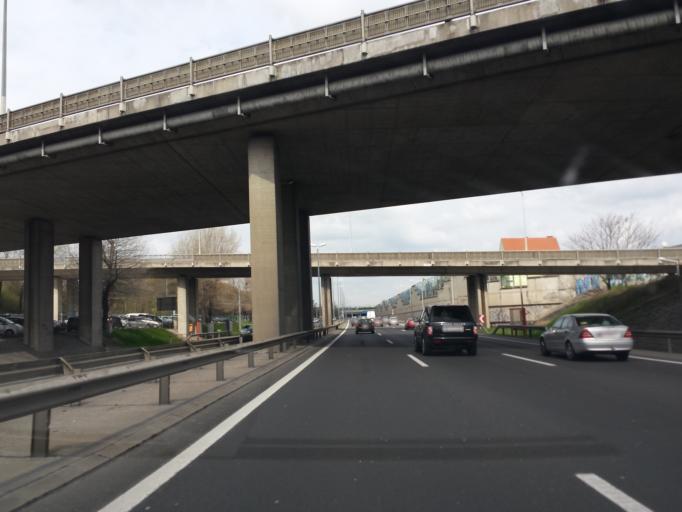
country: AT
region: Vienna
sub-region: Wien Stadt
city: Vienna
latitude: 48.2400
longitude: 16.4026
